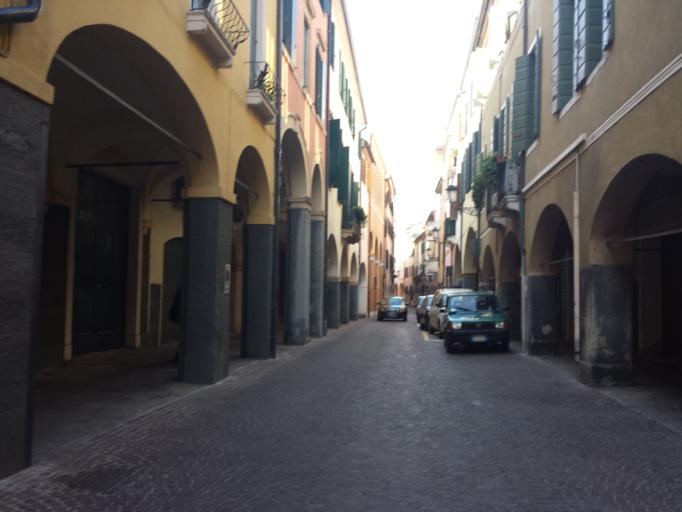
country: IT
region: Veneto
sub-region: Provincia di Padova
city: Padova
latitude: 45.4060
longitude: 11.8815
